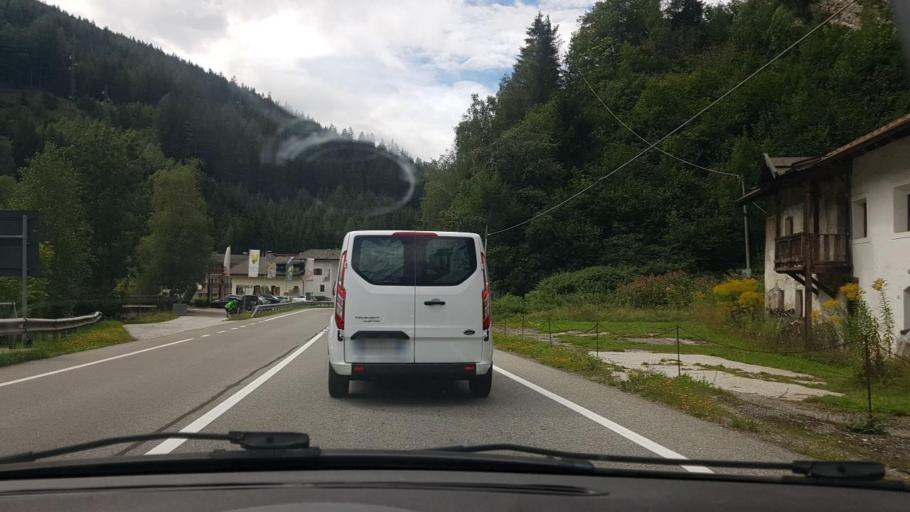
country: IT
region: Trentino-Alto Adige
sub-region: Bolzano
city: Brennero - Brenner
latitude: 46.9152
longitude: 11.4429
